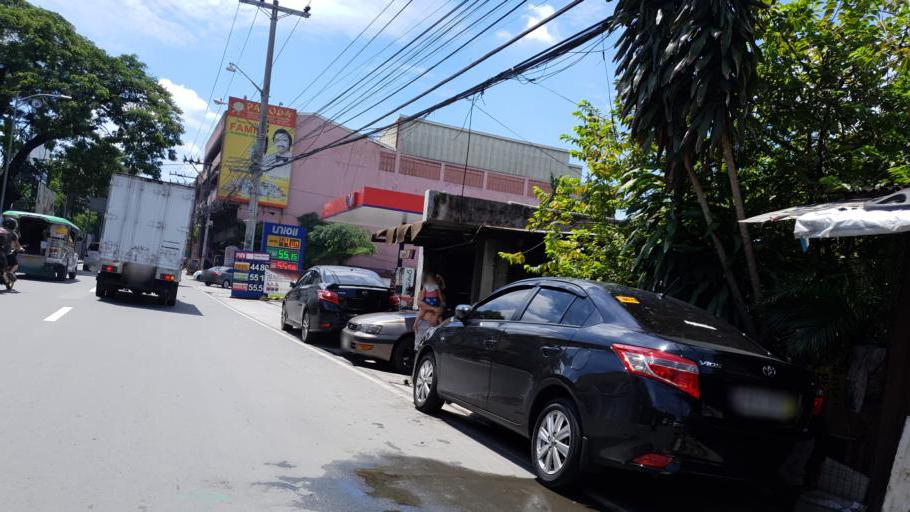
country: PH
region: Metro Manila
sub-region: San Juan
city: San Juan
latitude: 14.5993
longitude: 121.0143
